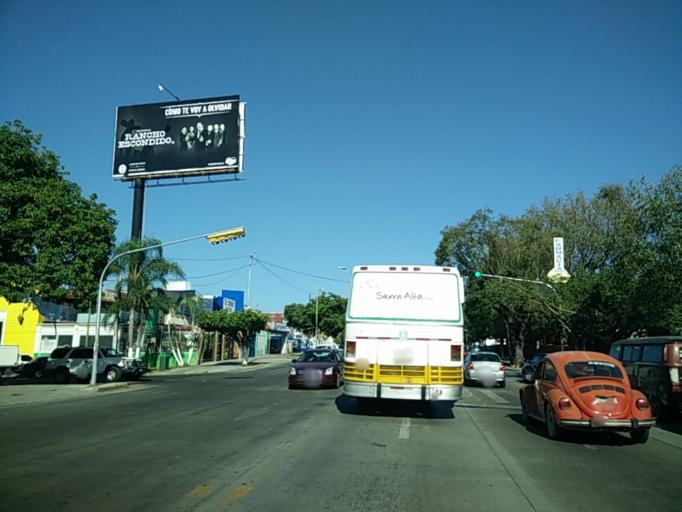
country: MX
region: Jalisco
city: Tlaquepaque
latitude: 20.6600
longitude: -103.3308
